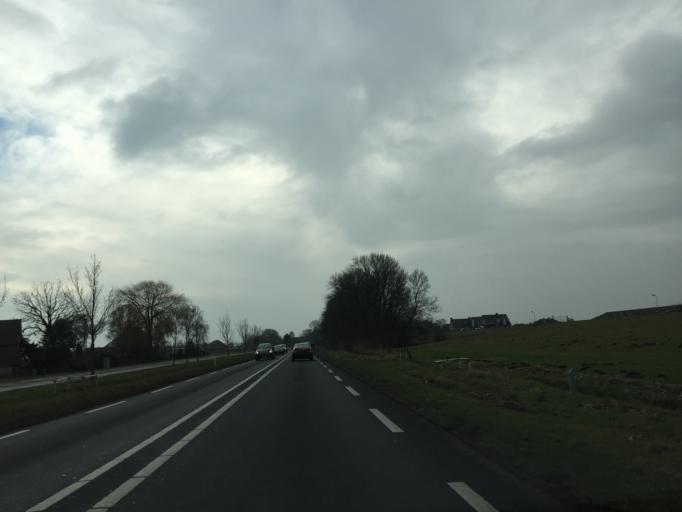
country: NL
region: South Holland
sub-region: Gemeente Lansingerland
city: Bleiswijk
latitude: 51.9947
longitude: 4.5952
